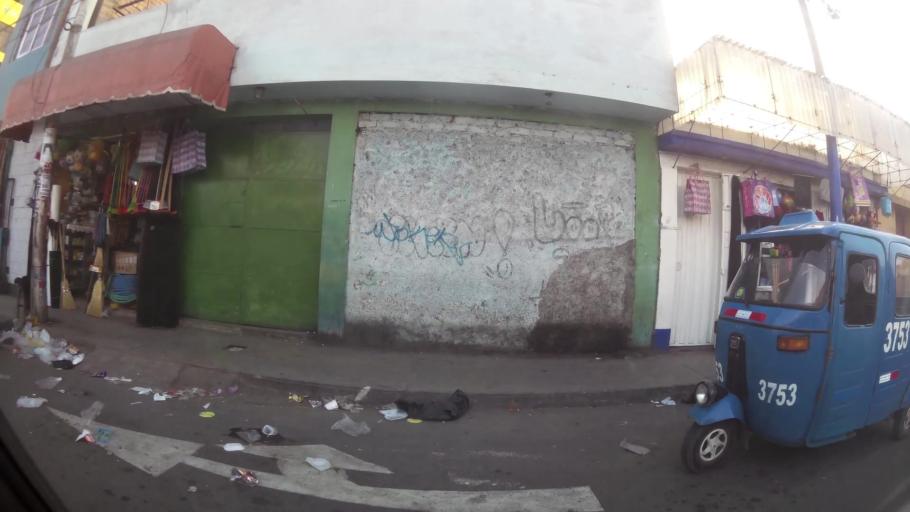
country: PE
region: Lima
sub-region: Huaura
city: Huacho
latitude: -11.1035
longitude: -77.6092
